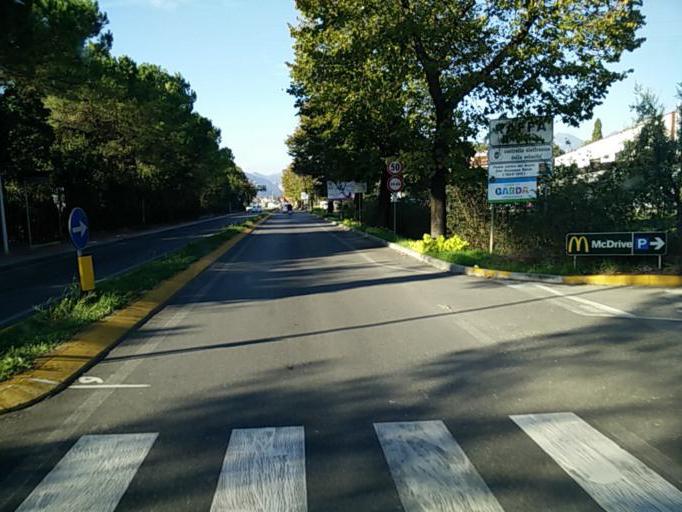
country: IT
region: Lombardy
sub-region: Provincia di Brescia
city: Raffa
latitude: 45.5654
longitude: 10.5318
